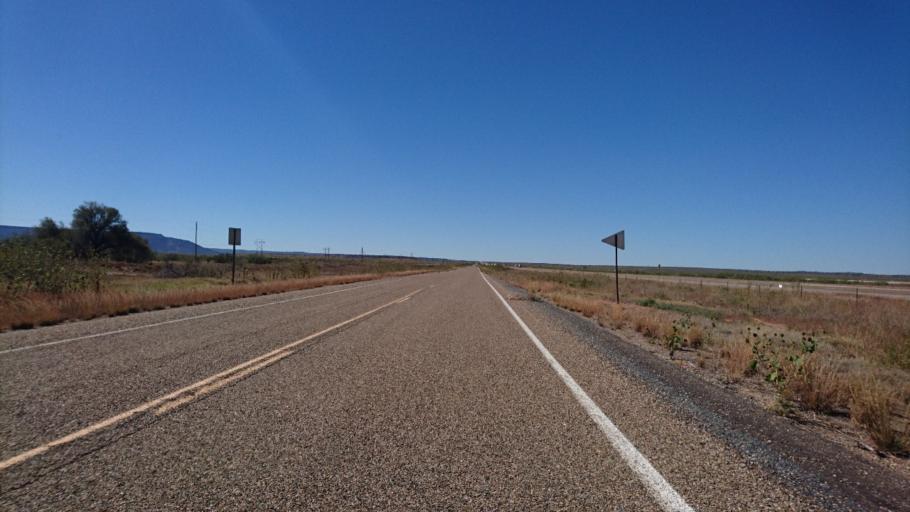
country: US
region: New Mexico
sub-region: Quay County
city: Tucumcari
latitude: 35.0911
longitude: -104.0780
